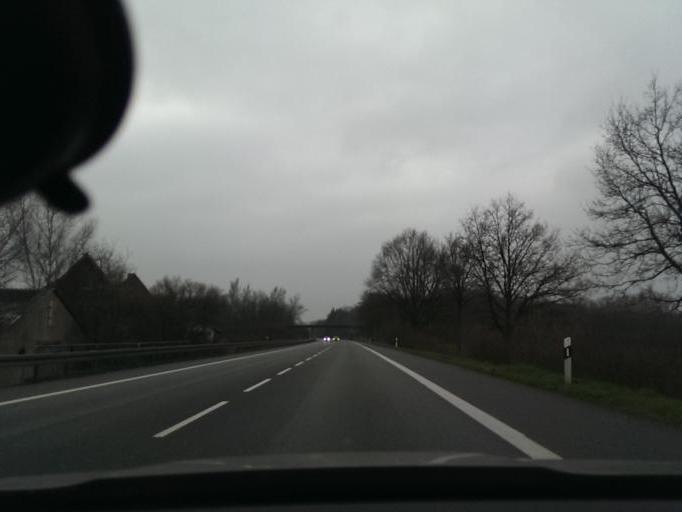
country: DE
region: North Rhine-Westphalia
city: Rietberg
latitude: 51.8046
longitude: 8.4095
